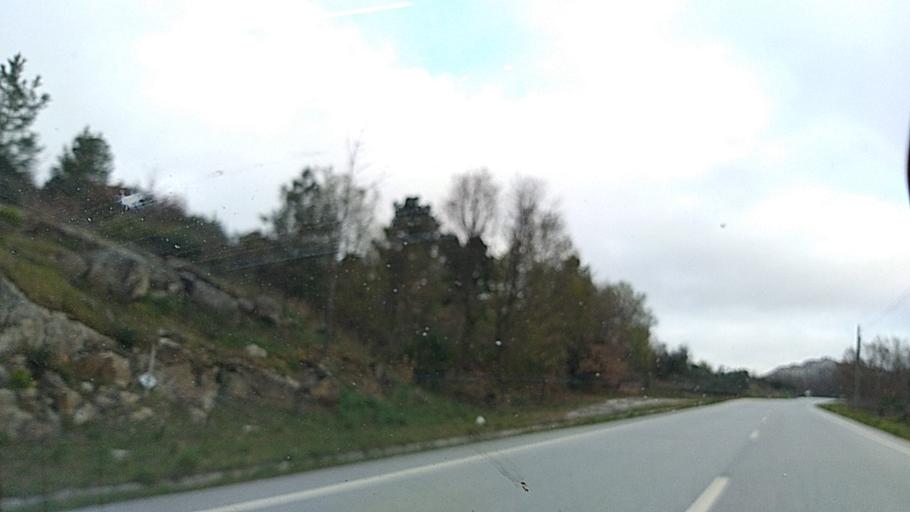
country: PT
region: Guarda
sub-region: Fornos de Algodres
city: Fornos de Algodres
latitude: 40.6496
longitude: -7.4890
